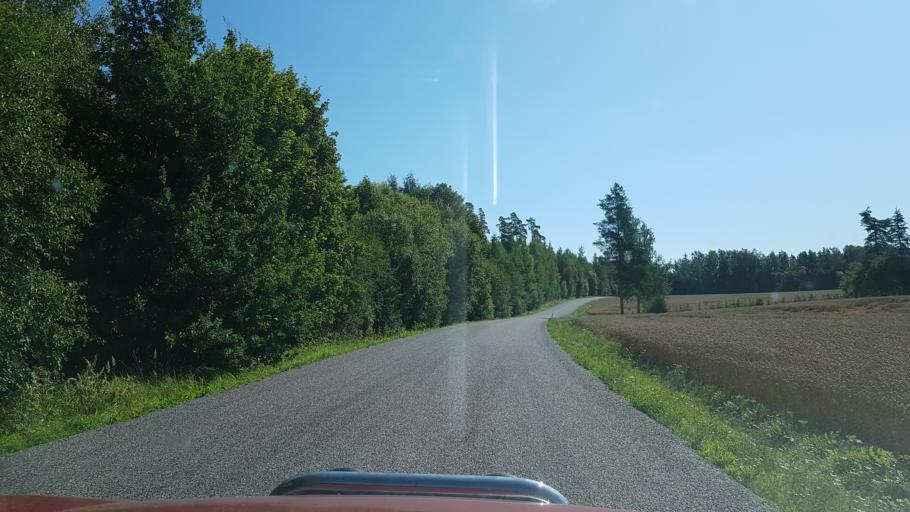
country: EE
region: Tartu
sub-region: Puhja vald
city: Puhja
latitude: 58.2567
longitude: 26.3221
